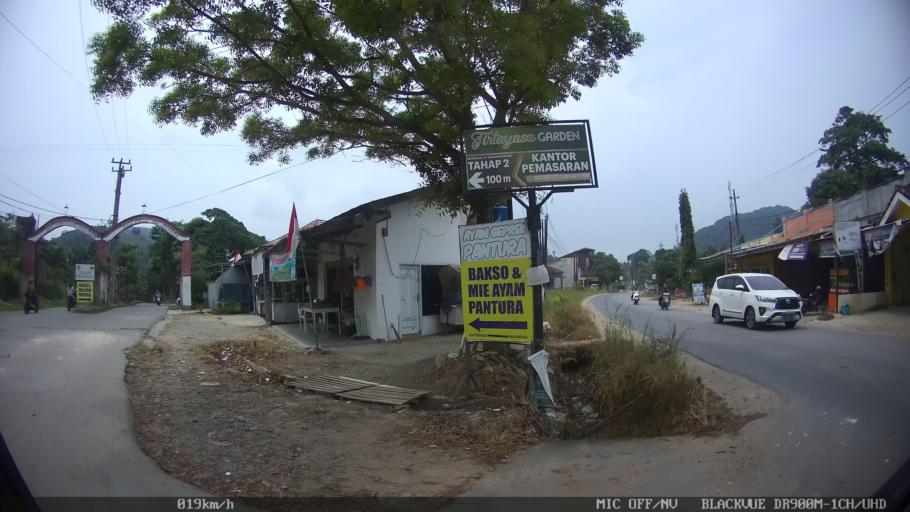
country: ID
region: Lampung
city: Kedaton
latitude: -5.4042
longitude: 105.3180
